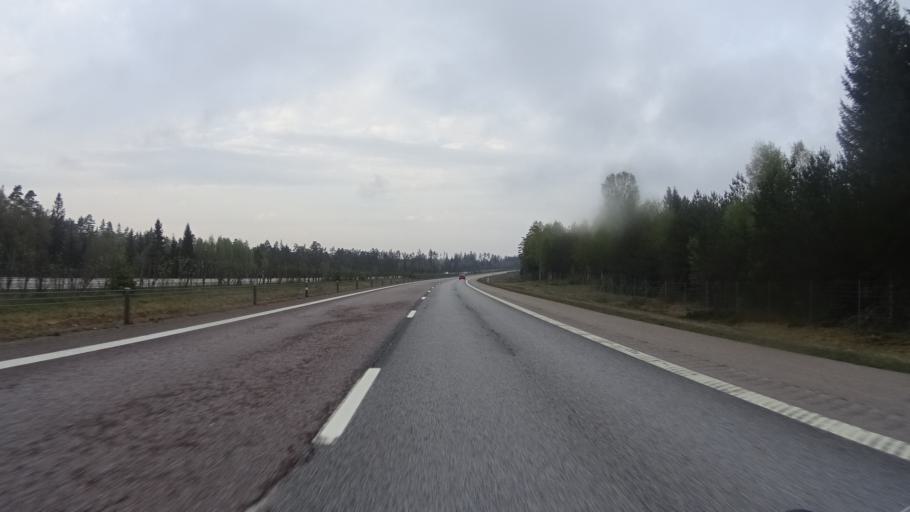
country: SE
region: Kronoberg
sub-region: Ljungby Kommun
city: Ljungby
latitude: 56.7414
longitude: 13.8545
